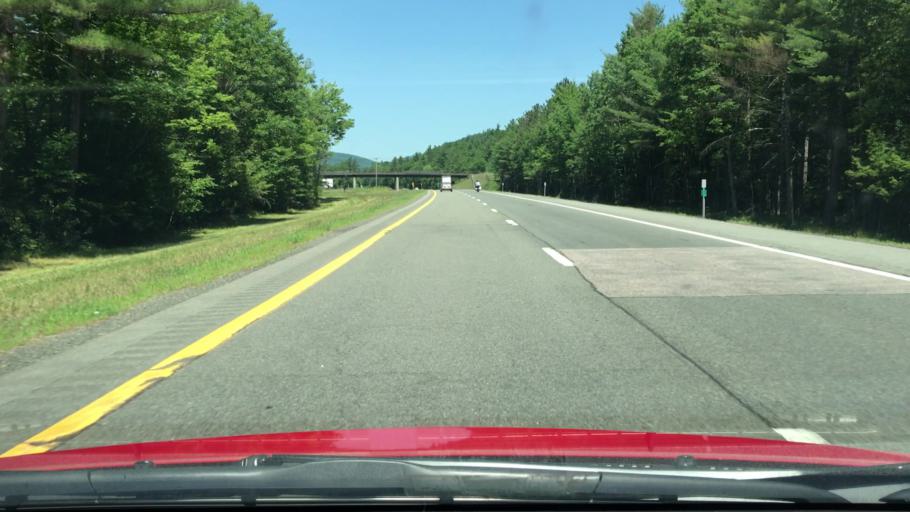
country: US
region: New York
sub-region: Essex County
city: Elizabethtown
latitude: 44.3228
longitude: -73.5285
